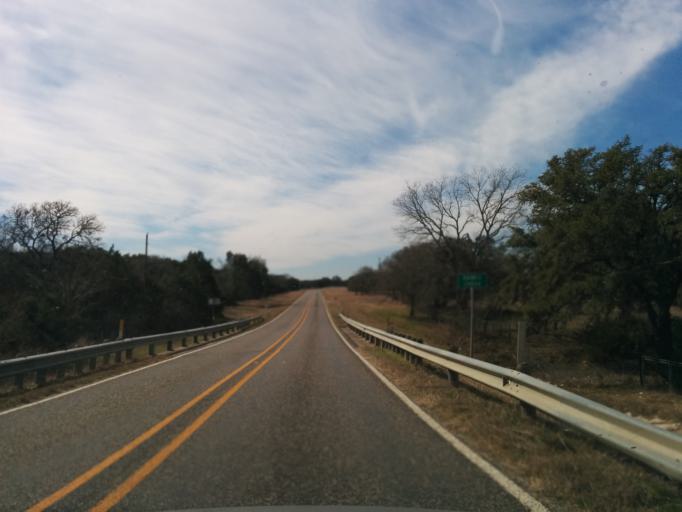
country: US
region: Texas
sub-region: Blanco County
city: Blanco
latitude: 29.9613
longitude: -98.5373
